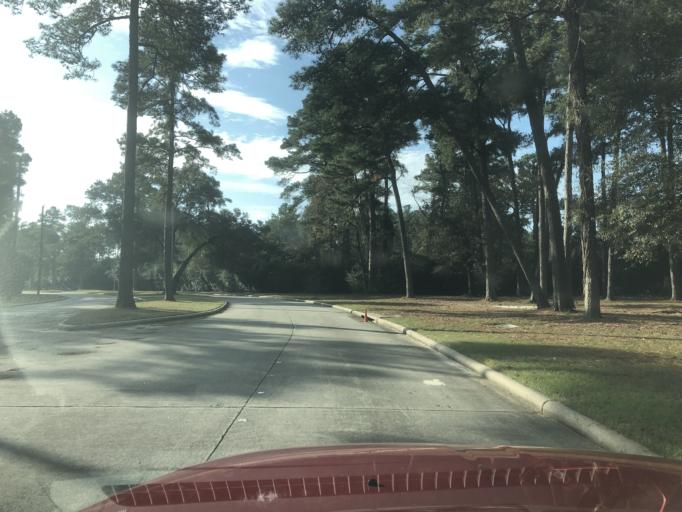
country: US
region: Texas
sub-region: Harris County
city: Spring
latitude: 30.0036
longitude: -95.4765
